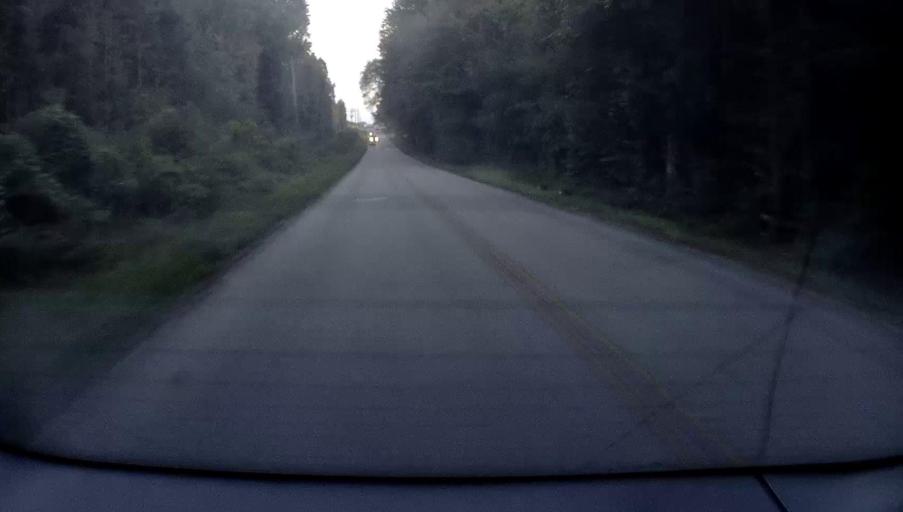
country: US
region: Georgia
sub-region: Butts County
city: Jackson
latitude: 33.2842
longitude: -84.0432
